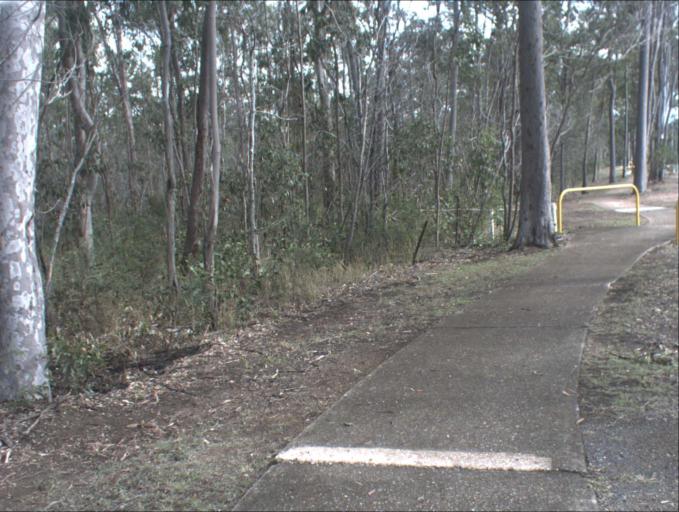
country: AU
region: Queensland
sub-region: Logan
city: Park Ridge South
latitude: -27.7083
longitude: 152.9767
